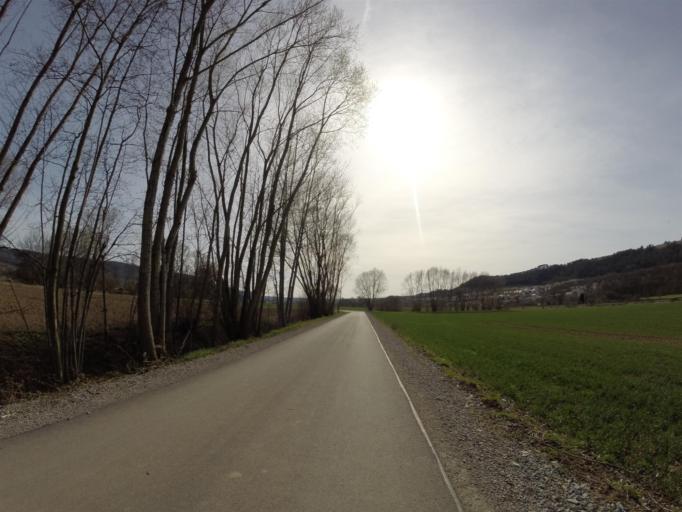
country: DE
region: Thuringia
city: Neuengonna
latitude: 50.9682
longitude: 11.6346
